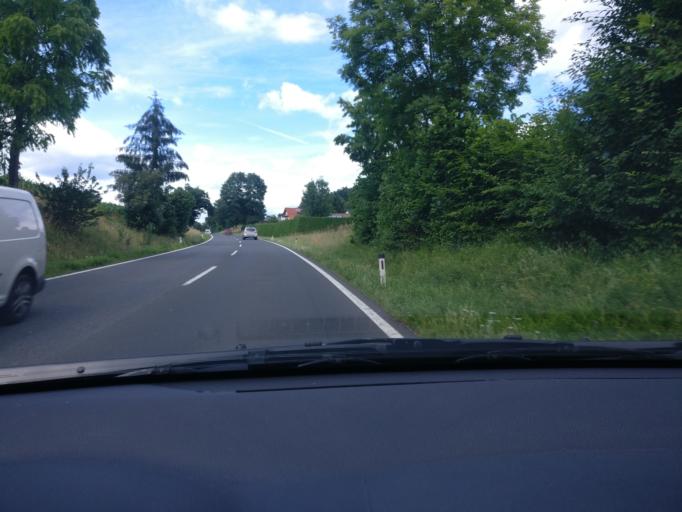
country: AT
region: Styria
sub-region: Politischer Bezirk Hartberg-Fuerstenfeld
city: Kaibing
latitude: 47.1988
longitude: 15.8411
